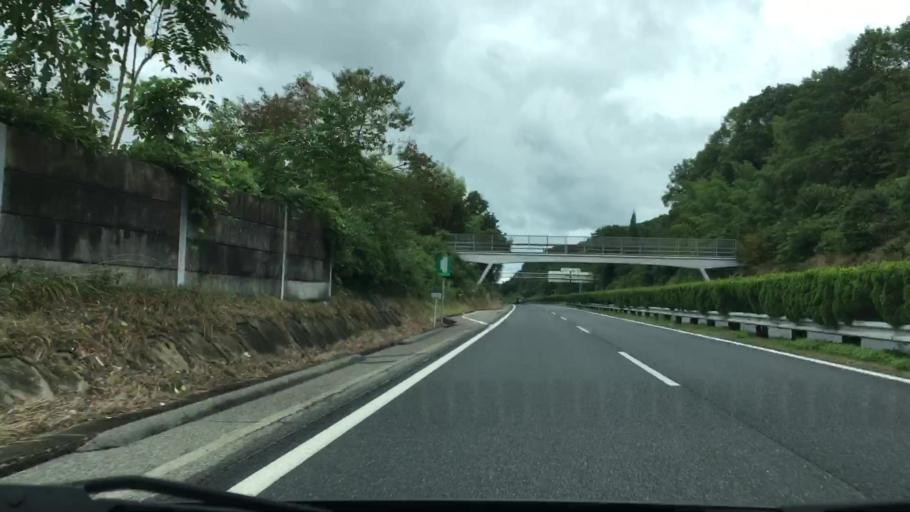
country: JP
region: Okayama
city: Tsuyama
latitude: 35.0401
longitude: 134.1270
